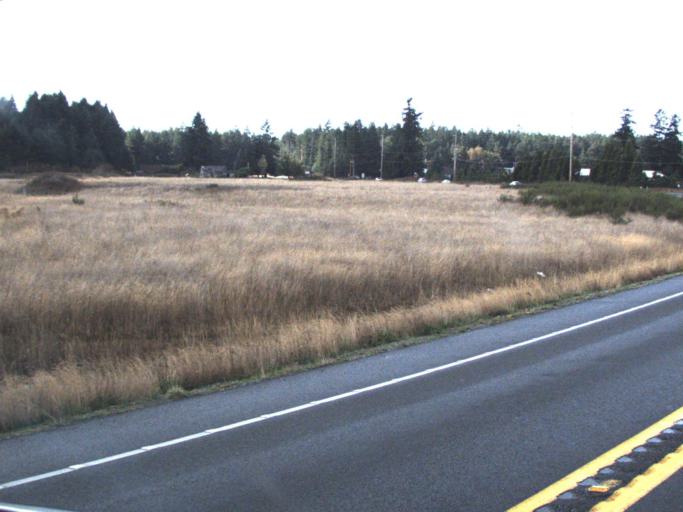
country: US
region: Washington
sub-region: Island County
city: Coupeville
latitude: 48.2074
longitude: -122.6359
